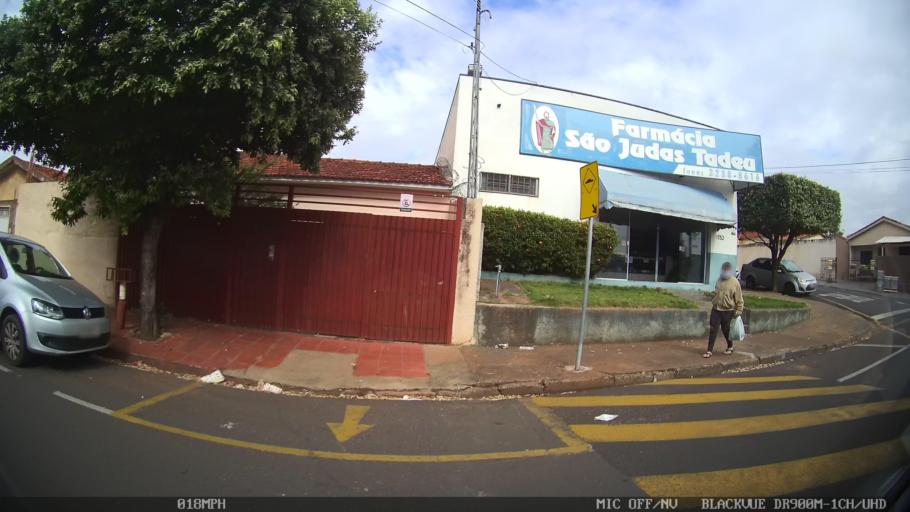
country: BR
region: Sao Paulo
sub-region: Sao Jose Do Rio Preto
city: Sao Jose do Rio Preto
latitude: -20.8208
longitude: -49.3535
